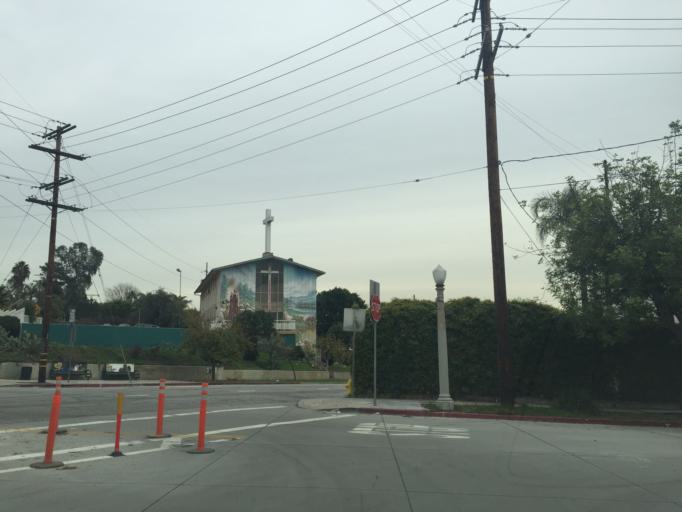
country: US
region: California
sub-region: Los Angeles County
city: Silver Lake
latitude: 34.1084
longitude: -118.2641
